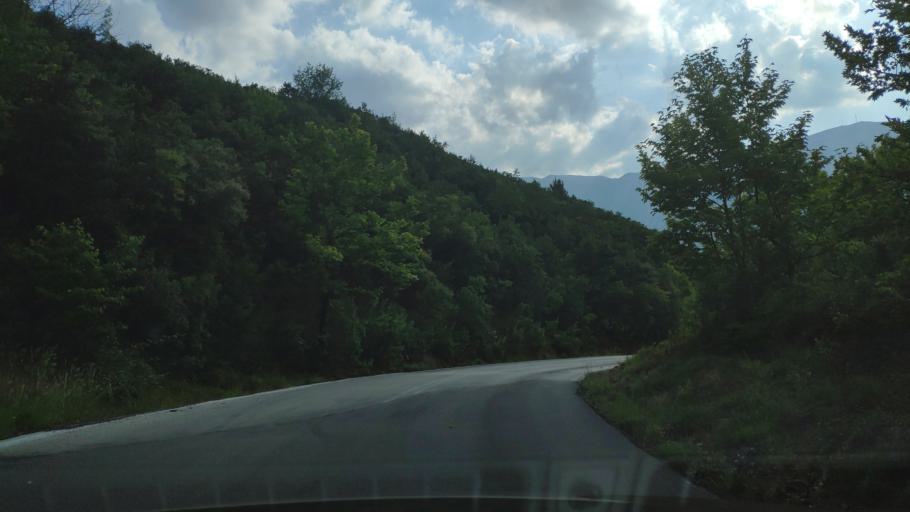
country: GR
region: Epirus
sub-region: Nomos Artas
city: Agios Dimitrios
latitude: 39.4574
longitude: 21.0546
